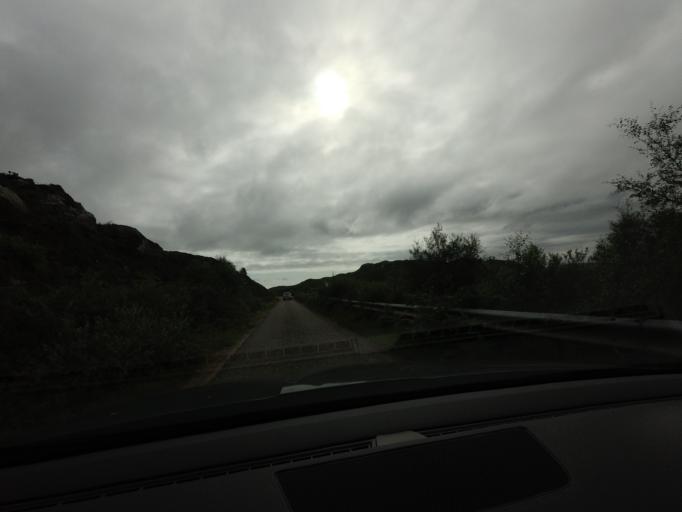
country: GB
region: Scotland
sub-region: Highland
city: Ullapool
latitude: 58.4373
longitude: -4.9634
